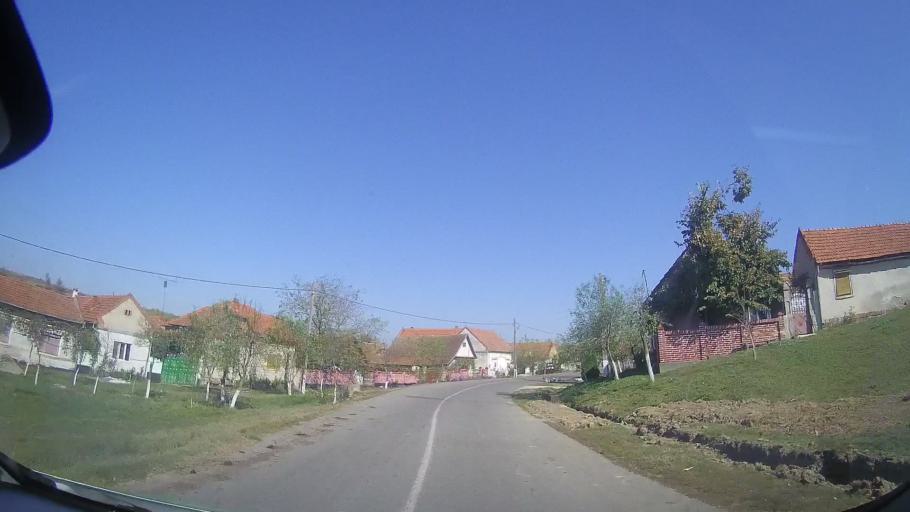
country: RO
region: Timis
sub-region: Comuna Balint
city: Balint
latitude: 45.8415
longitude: 21.8582
